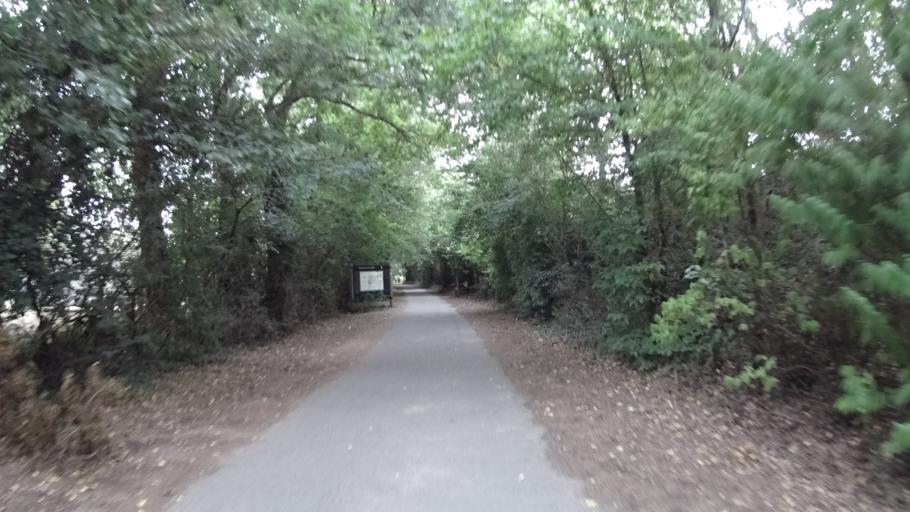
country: FR
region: Pays de la Loire
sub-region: Departement de la Loire-Atlantique
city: Thouare-sur-Loire
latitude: 47.2481
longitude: -1.4532
